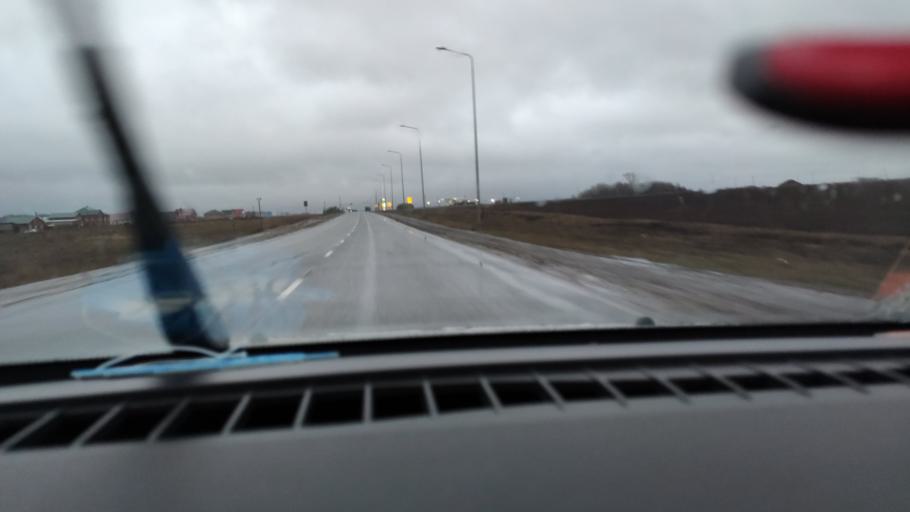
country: RU
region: Udmurtiya
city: Alnashi
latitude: 56.1744
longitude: 52.4699
